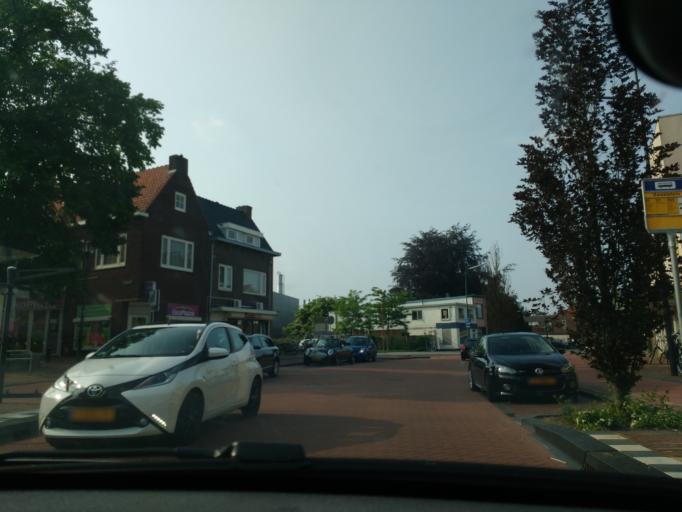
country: NL
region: Utrecht
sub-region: Gemeente Veenendaal
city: Veenendaal
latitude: 52.0288
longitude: 5.5596
